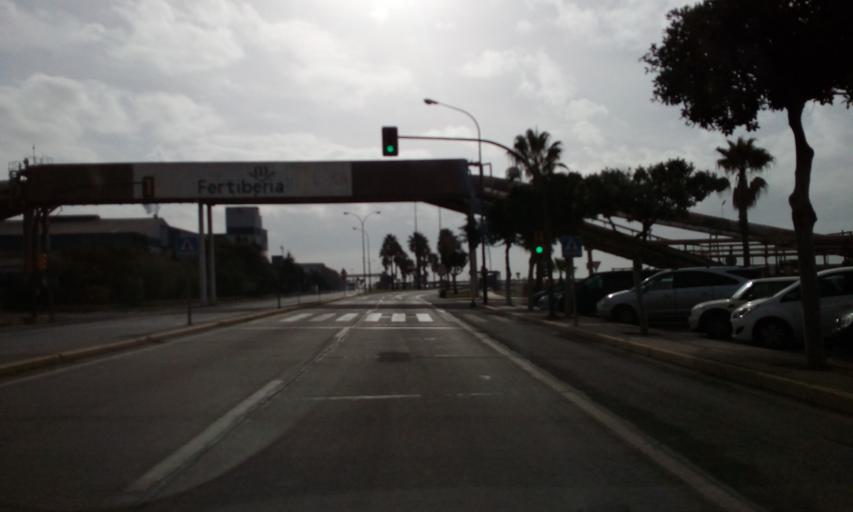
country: ES
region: Andalusia
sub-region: Provincia de Huelva
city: Huelva
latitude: 37.2302
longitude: -6.9527
